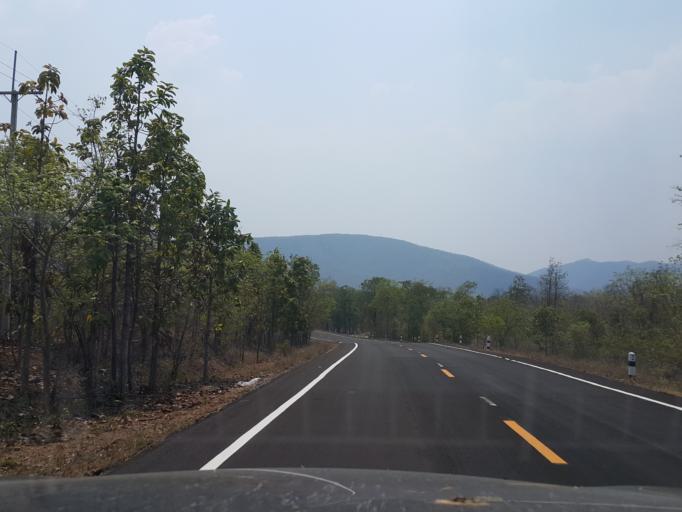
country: TH
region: Lampang
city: Mae Phrik
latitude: 17.4892
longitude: 99.0935
